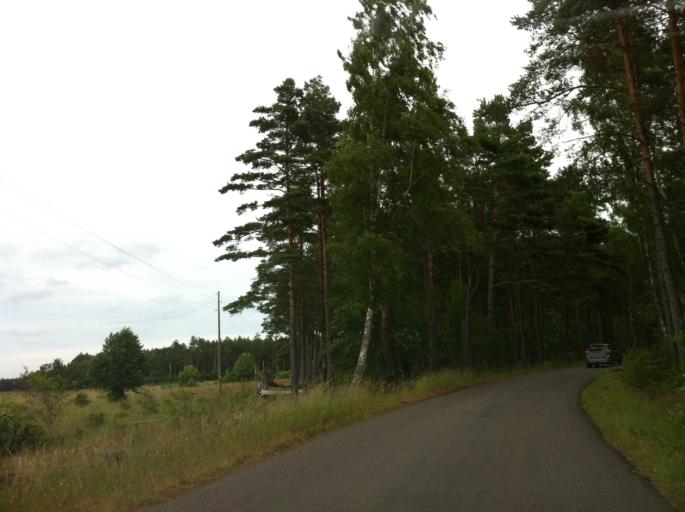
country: SE
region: Kalmar
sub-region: Vasterviks Kommun
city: Vaestervik
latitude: 57.3332
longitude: 17.1009
